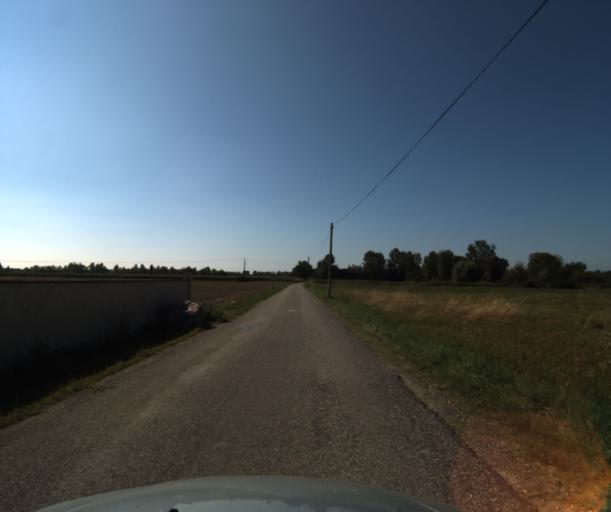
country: FR
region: Midi-Pyrenees
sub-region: Departement de la Haute-Garonne
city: Noe
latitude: 43.3664
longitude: 1.2681
